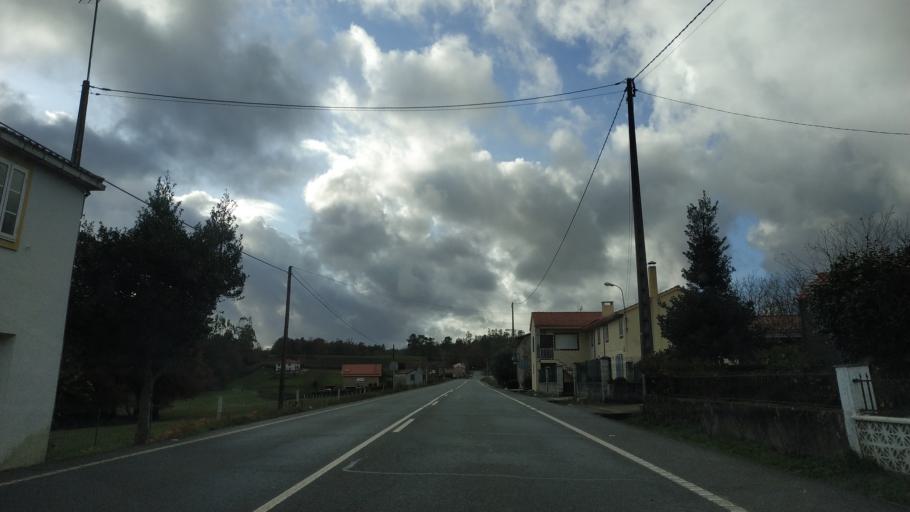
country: ES
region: Galicia
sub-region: Provincia da Coruna
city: Arzua
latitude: 42.8831
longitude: -8.1891
